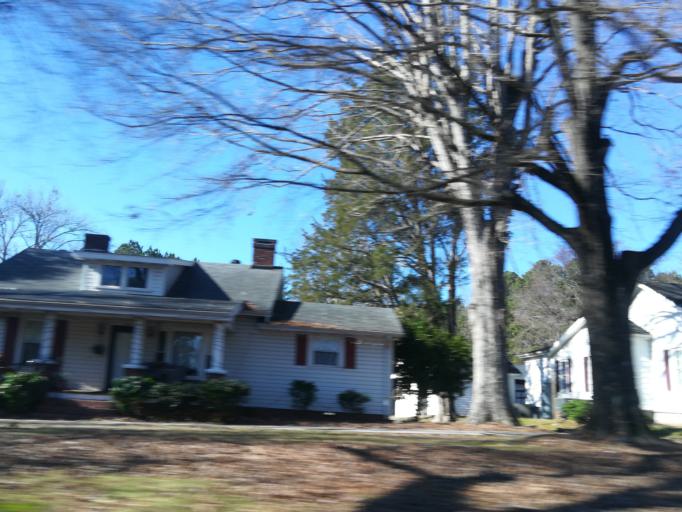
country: US
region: North Carolina
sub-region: Durham County
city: Durham
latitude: 36.0302
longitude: -78.9528
